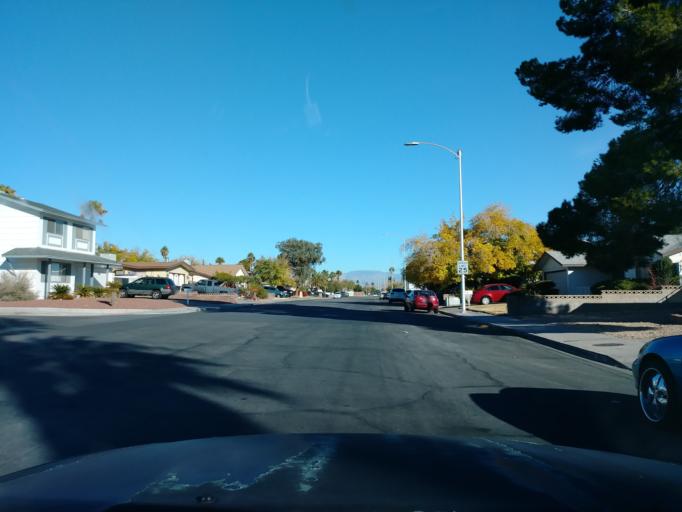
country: US
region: Nevada
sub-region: Clark County
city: Spring Valley
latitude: 36.1595
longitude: -115.2550
